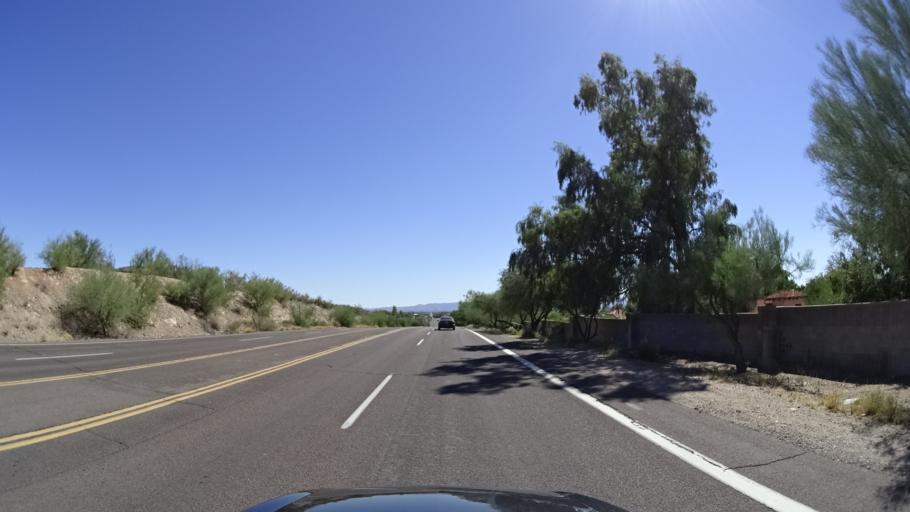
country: US
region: Arizona
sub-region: Maricopa County
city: Paradise Valley
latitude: 33.5296
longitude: -112.0131
